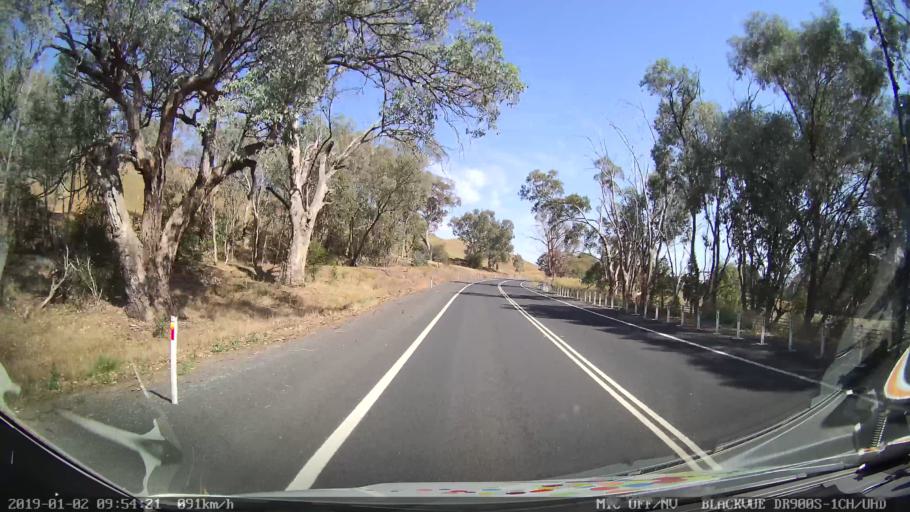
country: AU
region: New South Wales
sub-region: Tumut Shire
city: Tumut
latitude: -35.2365
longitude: 148.1968
